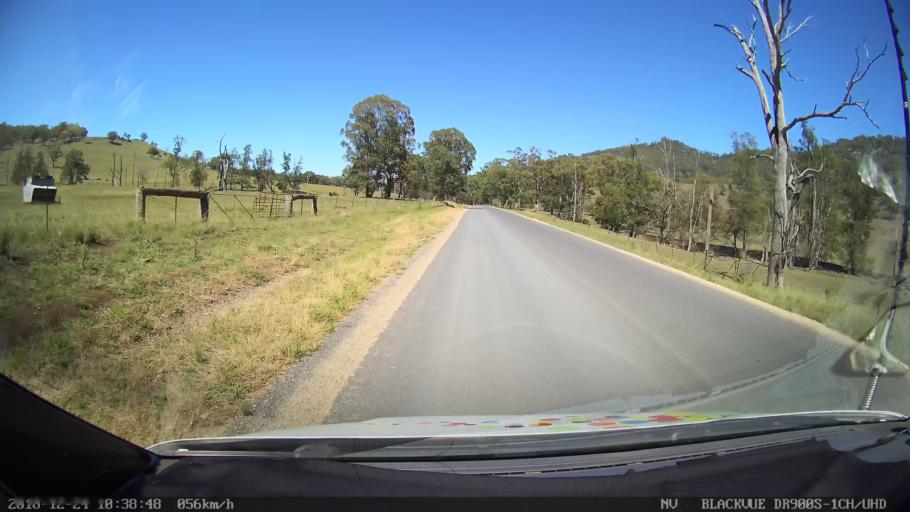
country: AU
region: New South Wales
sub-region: Upper Hunter Shire
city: Merriwa
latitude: -31.8496
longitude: 150.4798
